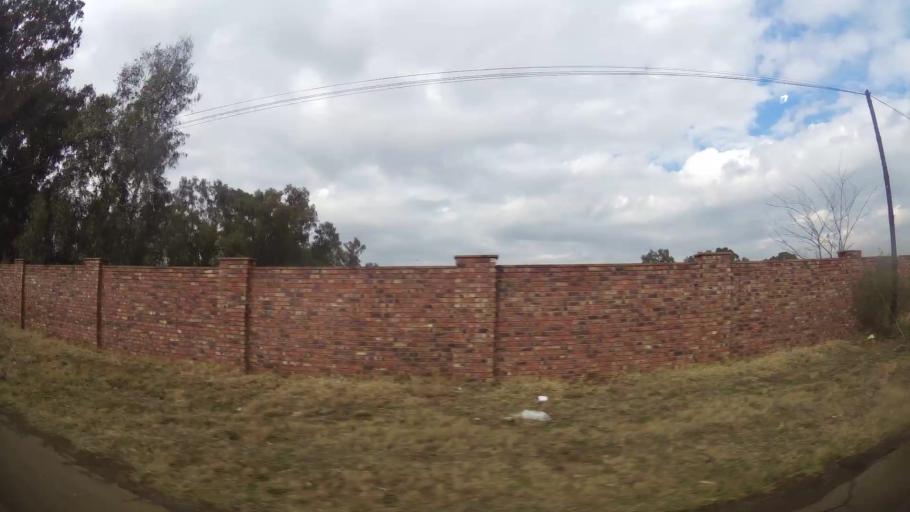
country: ZA
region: Gauteng
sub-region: Sedibeng District Municipality
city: Meyerton
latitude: -26.5878
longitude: 28.0083
